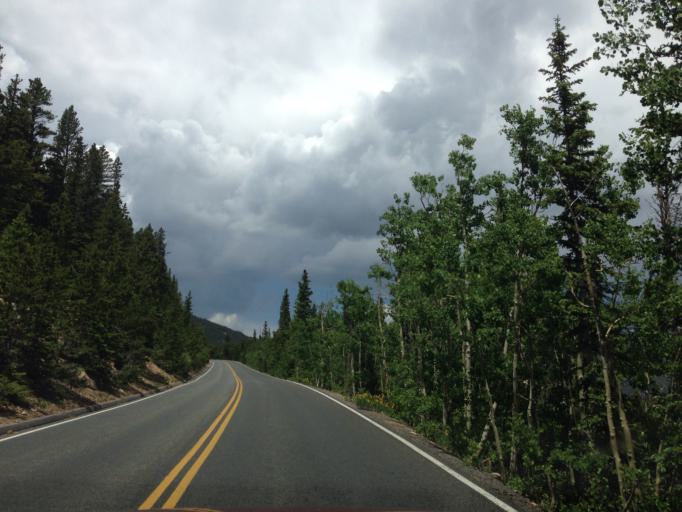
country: US
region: Colorado
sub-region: Larimer County
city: Estes Park
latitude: 40.3936
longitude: -105.6401
